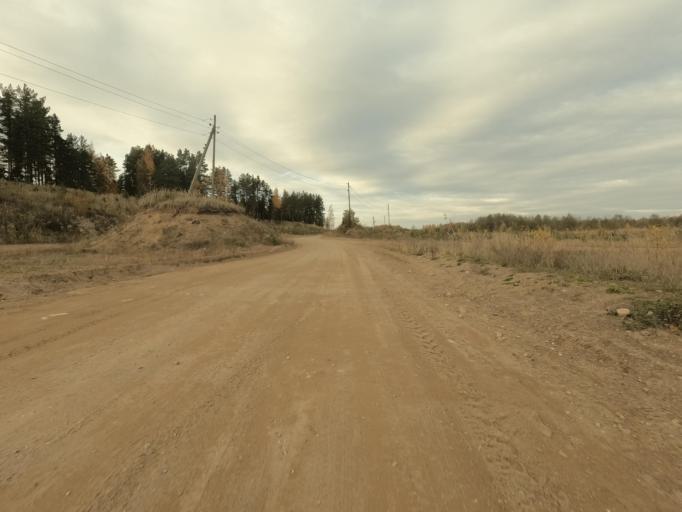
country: RU
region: Leningrad
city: Priladozhskiy
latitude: 59.7074
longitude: 31.3640
